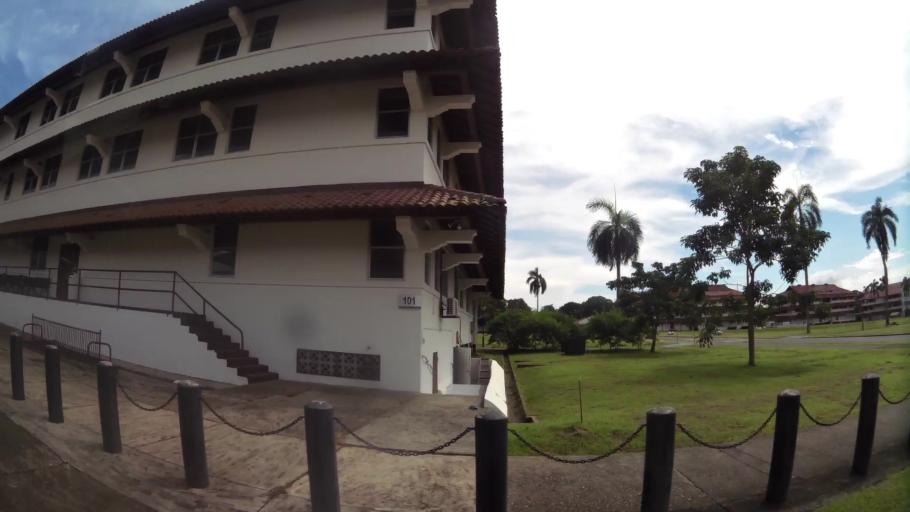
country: PA
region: Panama
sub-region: Distrito de Panama
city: Ancon
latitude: 9.0008
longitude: -79.5832
